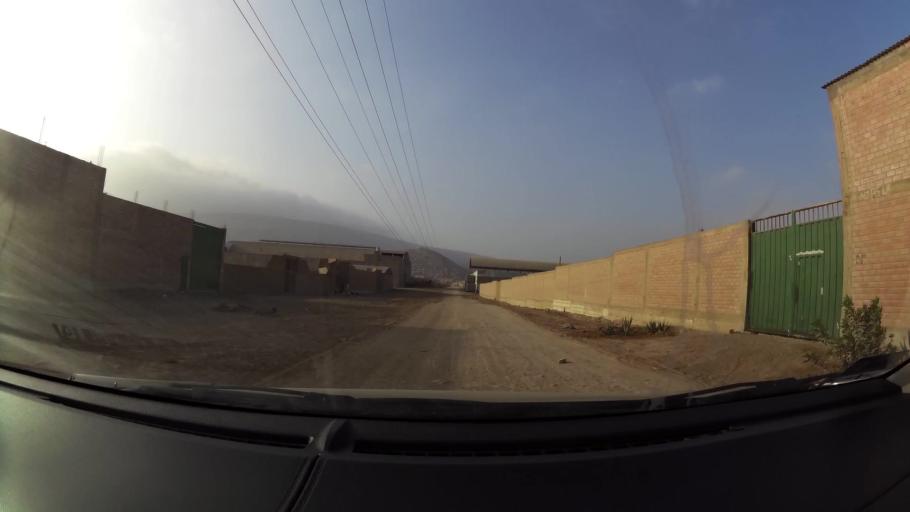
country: PE
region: Lima
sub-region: Lima
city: Santa Rosa
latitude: -11.7539
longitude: -77.1511
